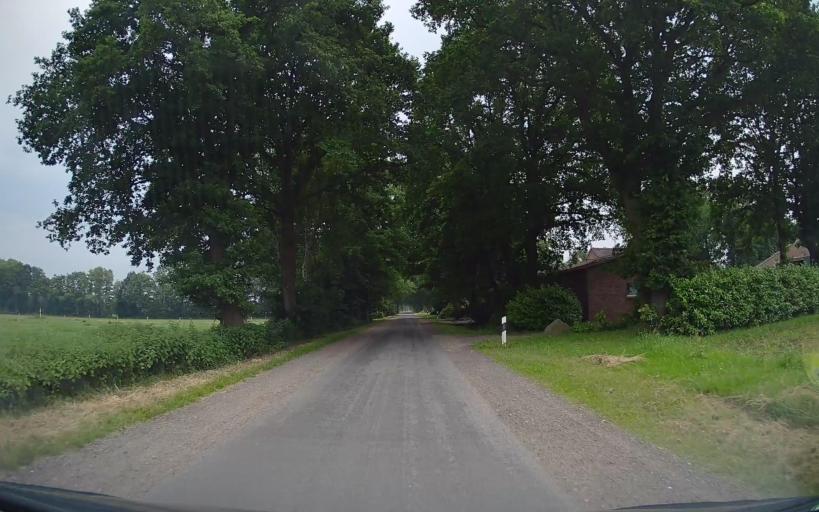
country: DE
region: Lower Saxony
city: Friesoythe
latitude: 53.0201
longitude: 7.9041
